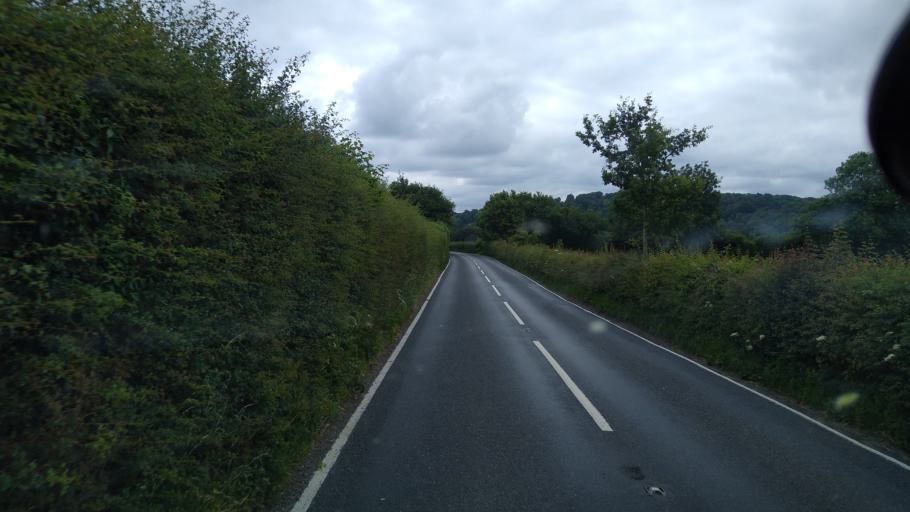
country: GB
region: England
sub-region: Hampshire
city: Alton
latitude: 51.1065
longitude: -0.9446
